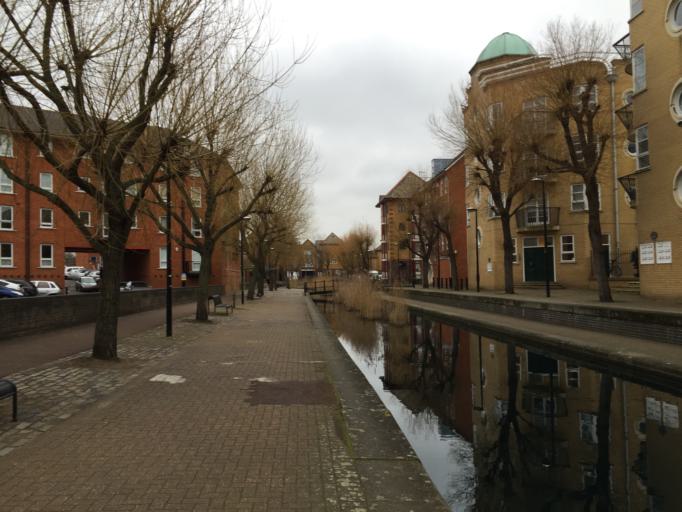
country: GB
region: England
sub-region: Greater London
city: Bethnal Green
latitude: 51.4999
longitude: -0.0459
